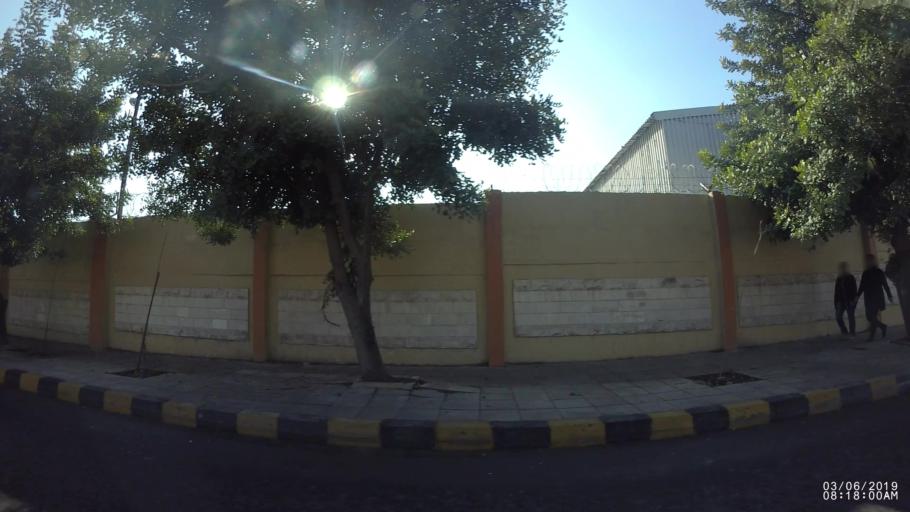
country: JO
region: Amman
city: Amman
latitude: 31.9753
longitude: 35.9765
